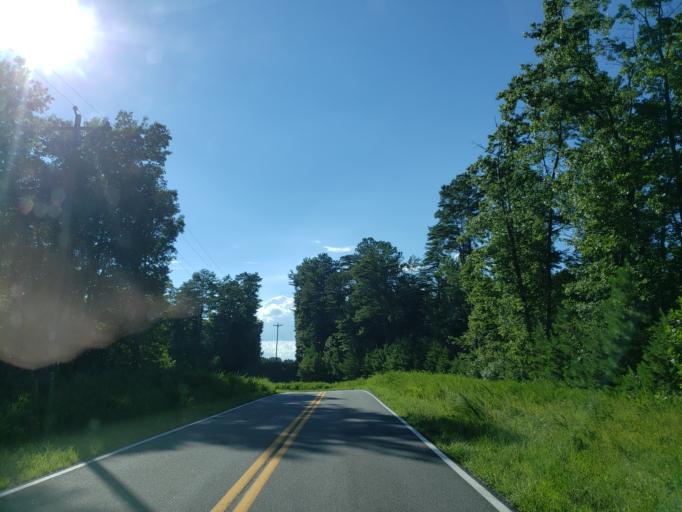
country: US
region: Georgia
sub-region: Bartow County
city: Rydal
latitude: 34.3541
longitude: -84.6027
